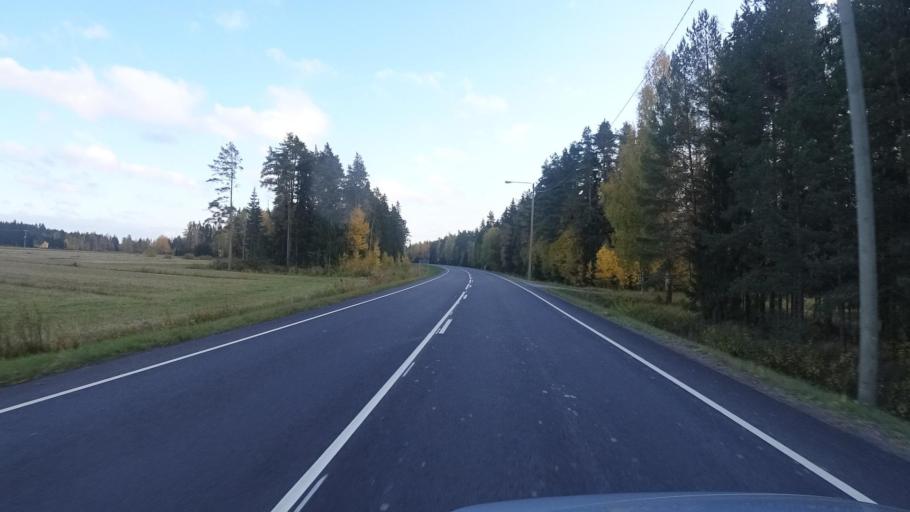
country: FI
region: Satakunta
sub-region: Rauma
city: Koeylioe
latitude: 61.0955
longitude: 22.2389
